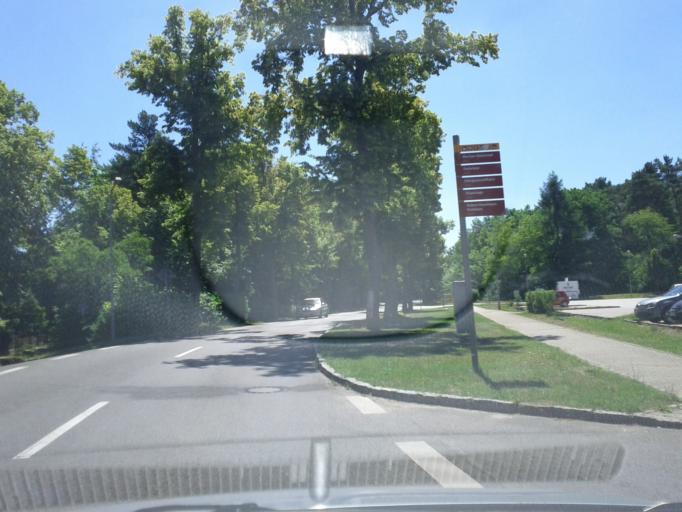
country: DE
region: Brandenburg
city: Grunheide
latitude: 52.4210
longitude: 13.8229
